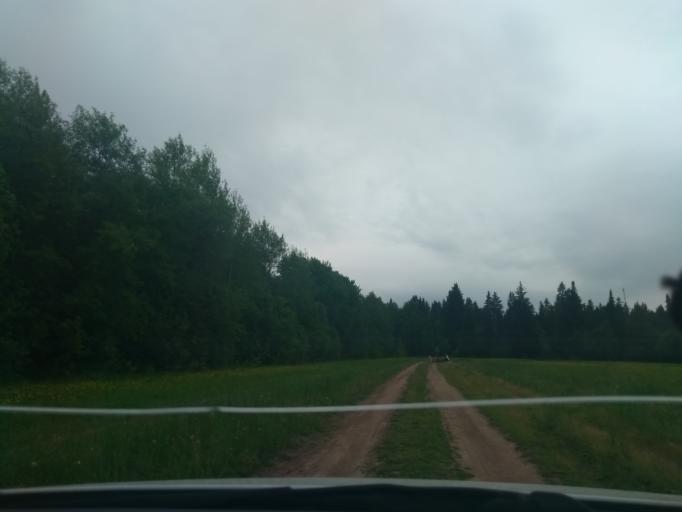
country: RU
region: Perm
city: Perm
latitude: 57.9861
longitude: 56.3324
